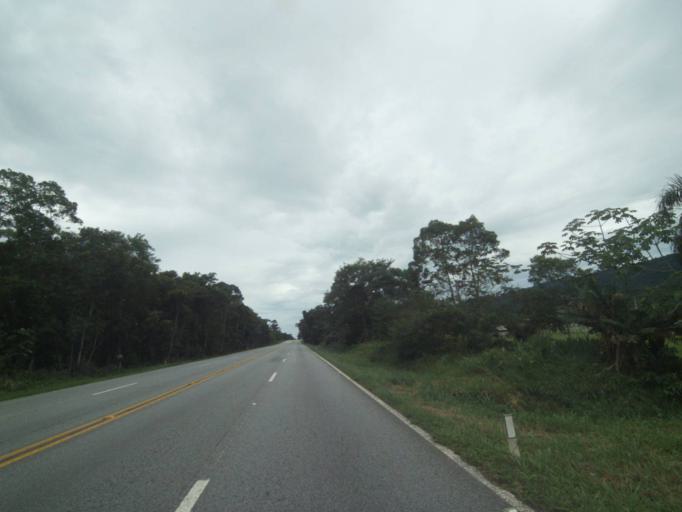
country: BR
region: Parana
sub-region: Pontal Do Parana
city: Pontal do Parana
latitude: -25.6328
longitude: -48.5944
